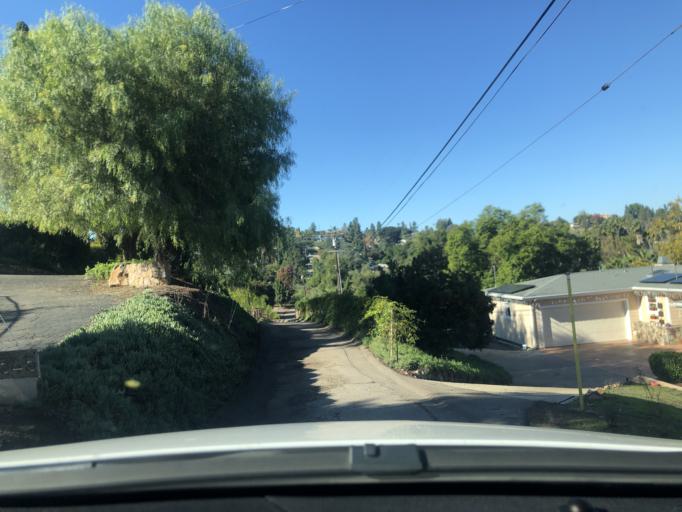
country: US
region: California
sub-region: San Diego County
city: Rancho San Diego
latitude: 32.7715
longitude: -116.9430
